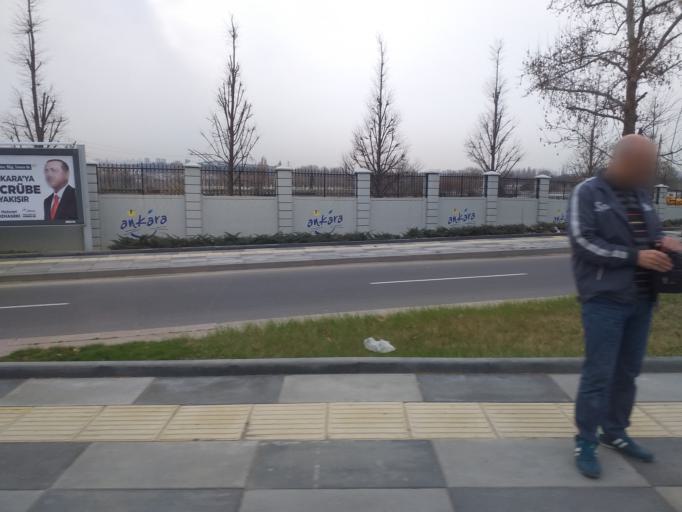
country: TR
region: Ankara
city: Ankara
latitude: 39.9529
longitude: 32.8215
